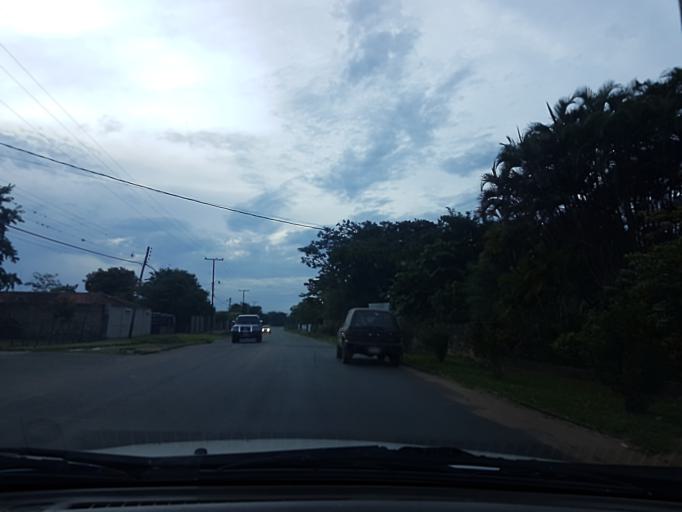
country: PY
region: Central
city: San Lorenzo
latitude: -25.2648
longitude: -57.4758
